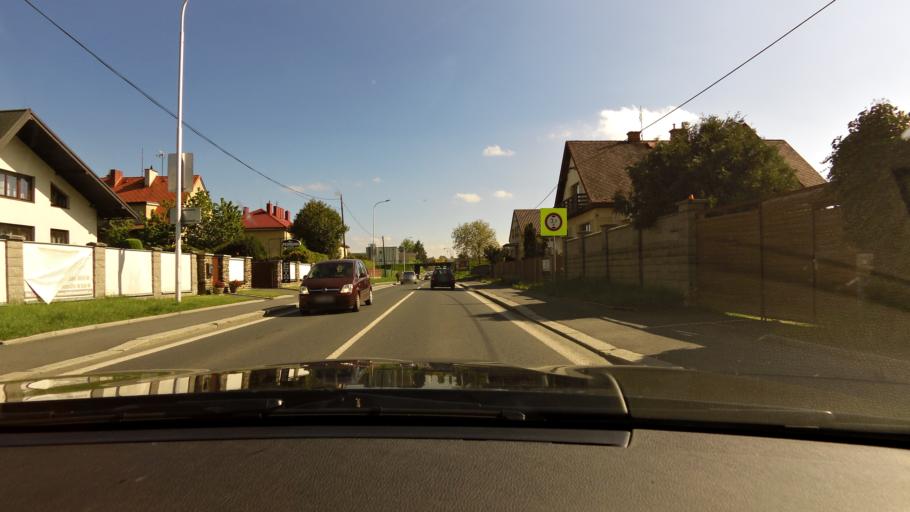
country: CZ
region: Plzensky
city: Klatovy
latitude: 49.3866
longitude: 13.2966
